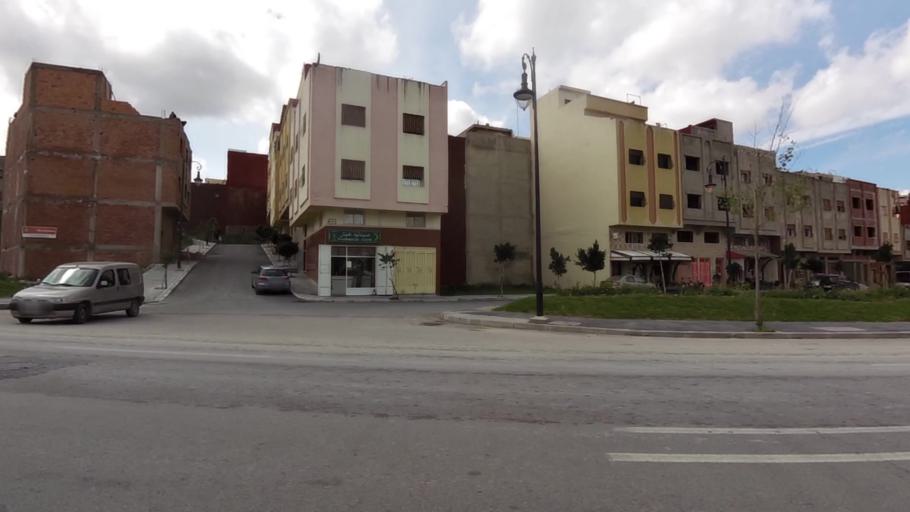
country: MA
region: Tanger-Tetouan
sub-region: Tanger-Assilah
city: Tangier
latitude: 35.7639
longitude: -5.7560
